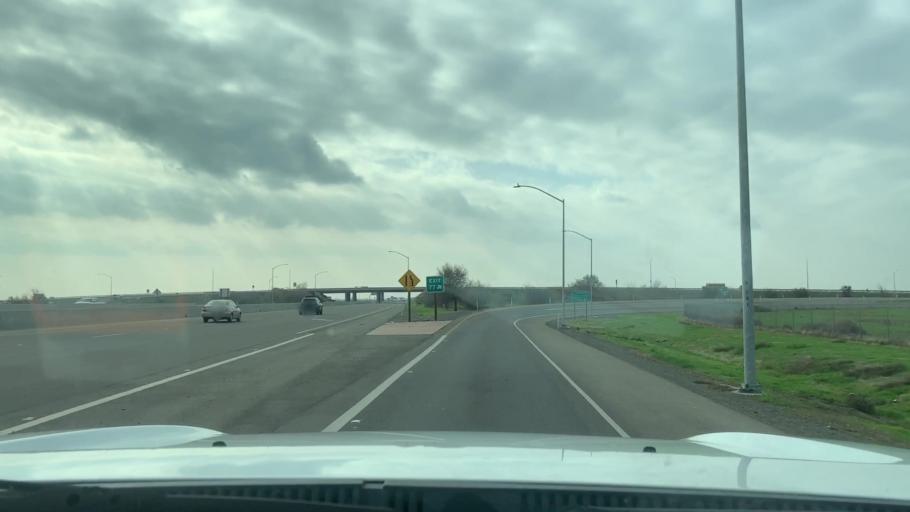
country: US
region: California
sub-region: Kings County
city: Lemoore
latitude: 36.2841
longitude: -119.8045
